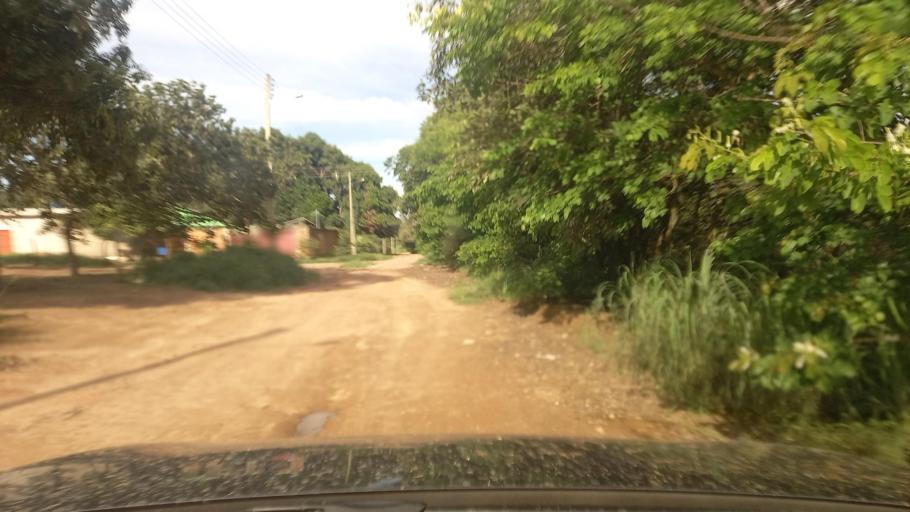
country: BR
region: Goias
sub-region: Cavalcante
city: Cavalcante
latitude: -13.8015
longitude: -47.4432
